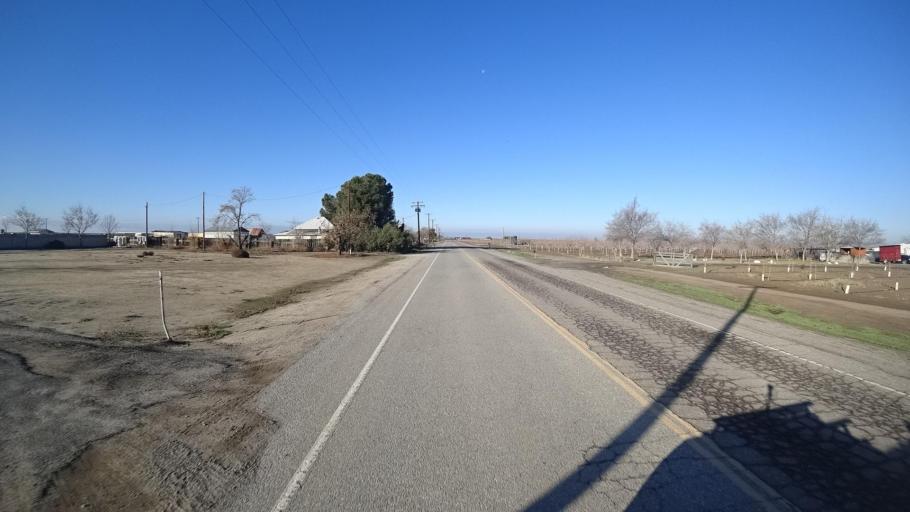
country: US
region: California
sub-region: Kern County
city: Delano
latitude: 35.7757
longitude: -119.3416
